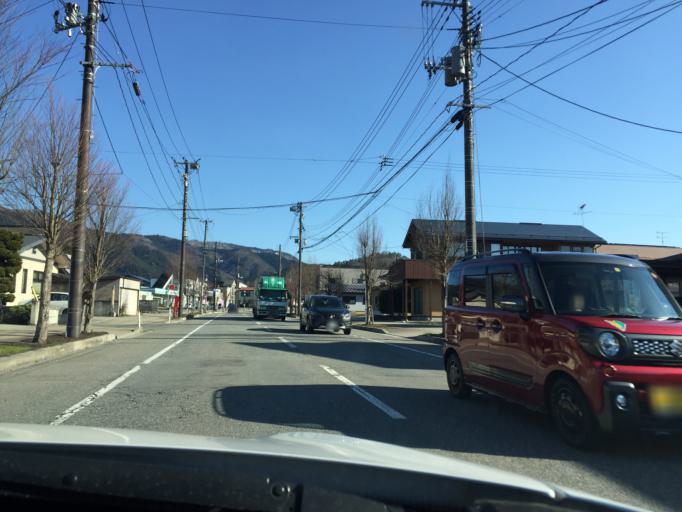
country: JP
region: Yamagata
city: Nagai
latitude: 38.1877
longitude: 140.1006
